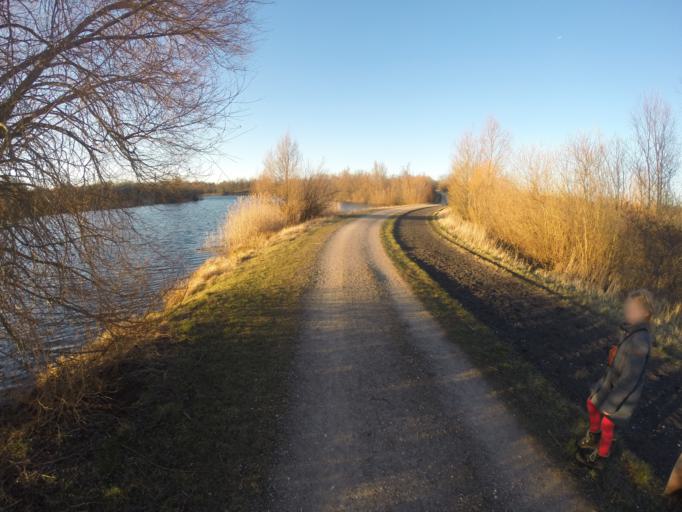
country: DK
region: Capital Region
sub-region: Hoje-Taastrup Kommune
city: Flong
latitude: 55.6345
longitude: 12.1867
